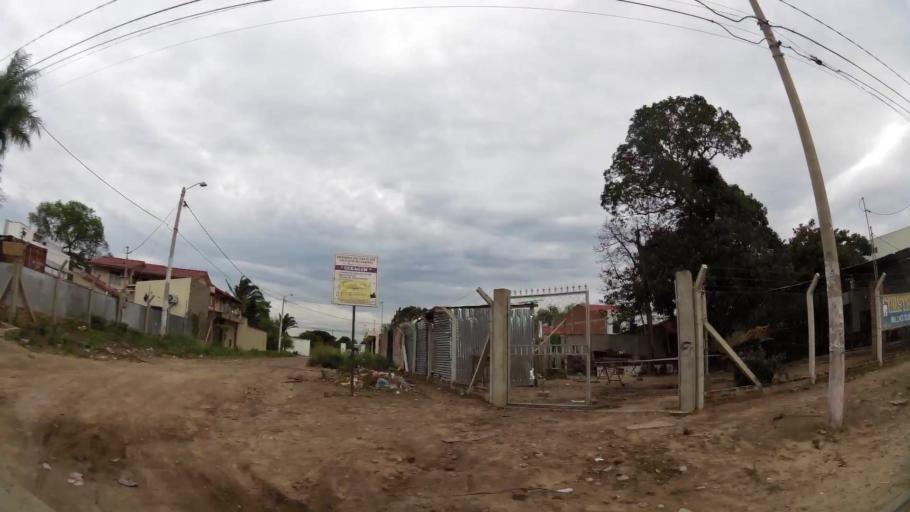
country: BO
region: Santa Cruz
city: Santa Cruz de la Sierra
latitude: -17.7391
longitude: -63.1563
